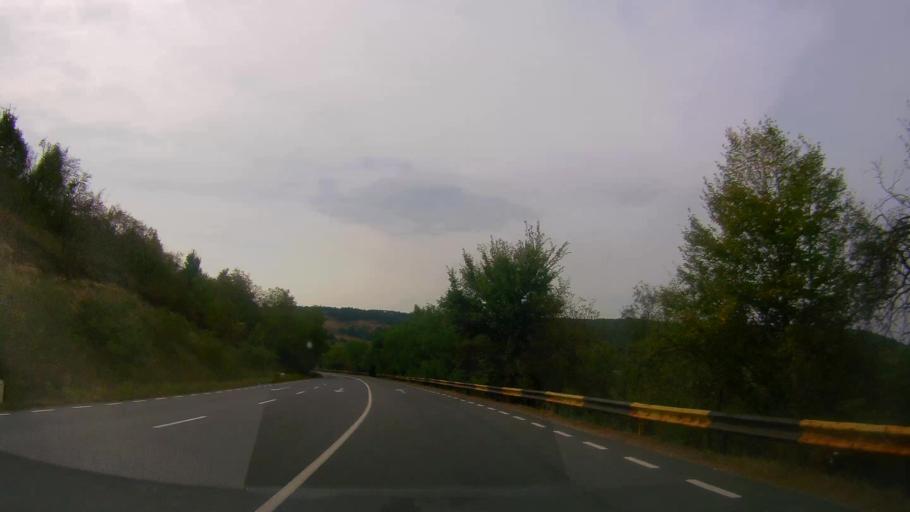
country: RO
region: Salaj
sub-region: Comuna Treznea
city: Treznea
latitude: 47.1276
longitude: 23.1292
